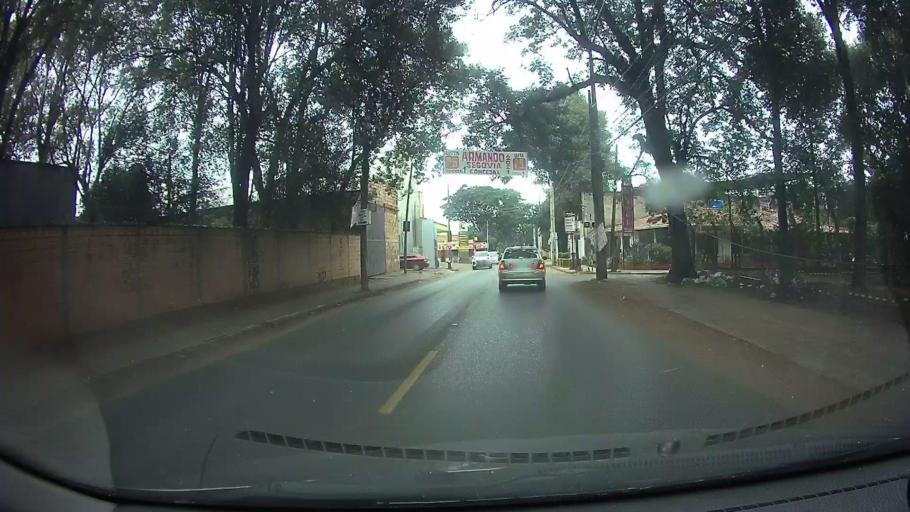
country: PY
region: Central
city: Villa Elisa
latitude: -25.3459
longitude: -57.5702
